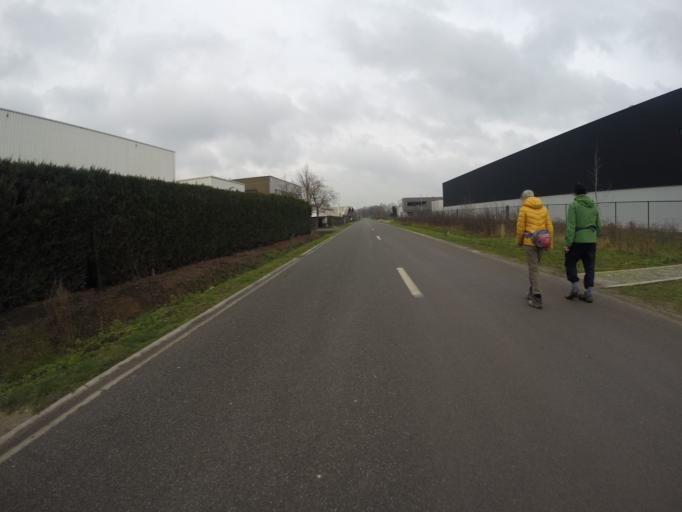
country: BE
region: Flanders
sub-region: Provincie West-Vlaanderen
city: Beernem
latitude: 51.1227
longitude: 3.3478
